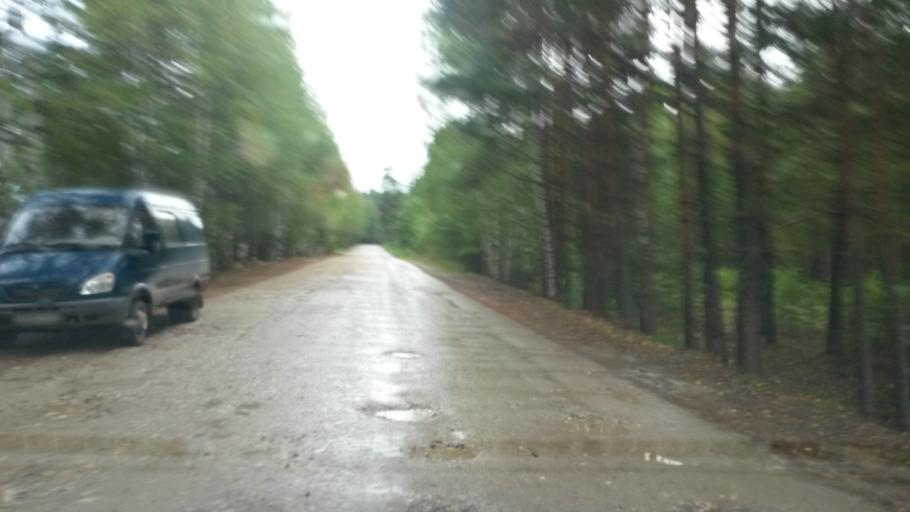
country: RU
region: Ivanovo
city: Zarechnyy
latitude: 57.5025
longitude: 42.2983
